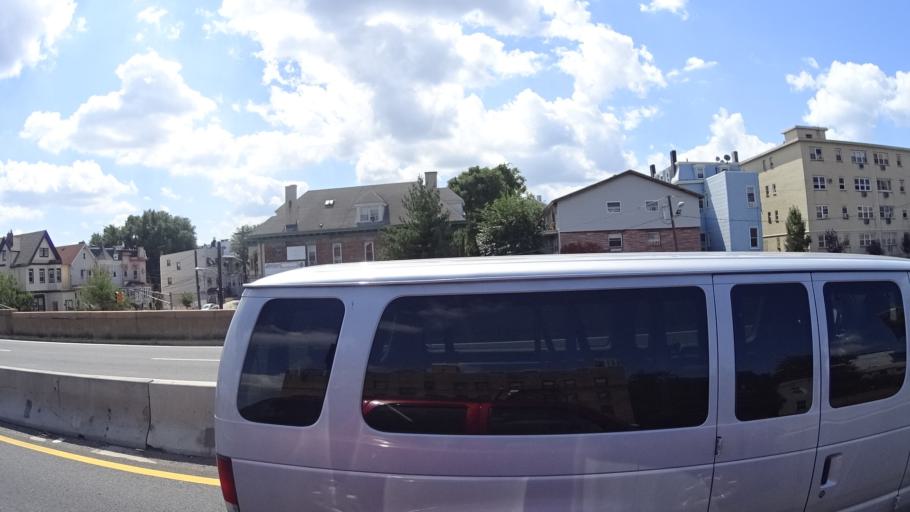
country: US
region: New Jersey
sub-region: Hudson County
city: Weehawken
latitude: 40.7692
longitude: -74.0246
